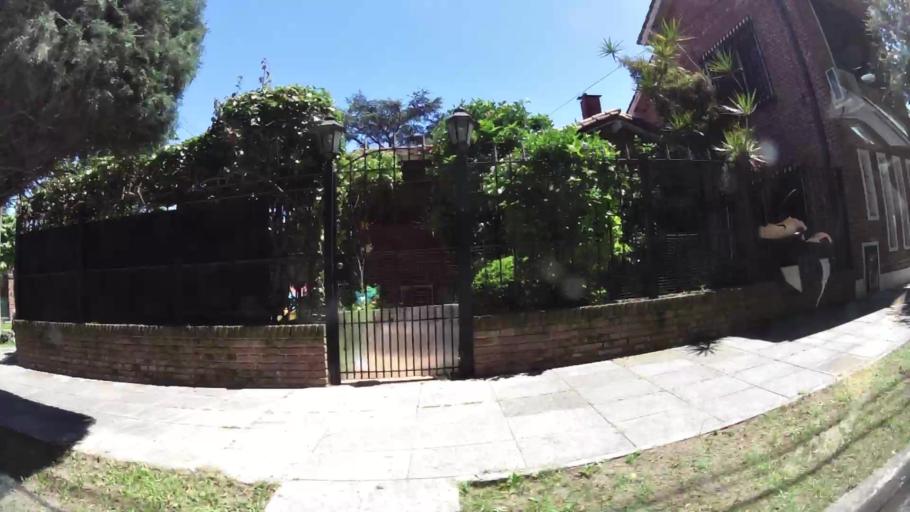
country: AR
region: Buenos Aires
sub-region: Partido de General San Martin
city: General San Martin
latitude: -34.5623
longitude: -58.5389
